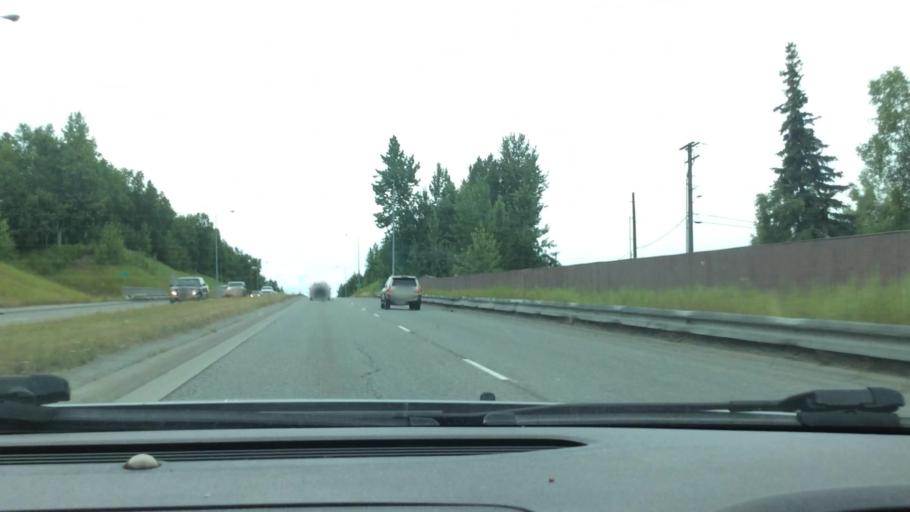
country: US
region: Alaska
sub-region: Anchorage Municipality
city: Anchorage
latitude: 61.2020
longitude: -149.7783
